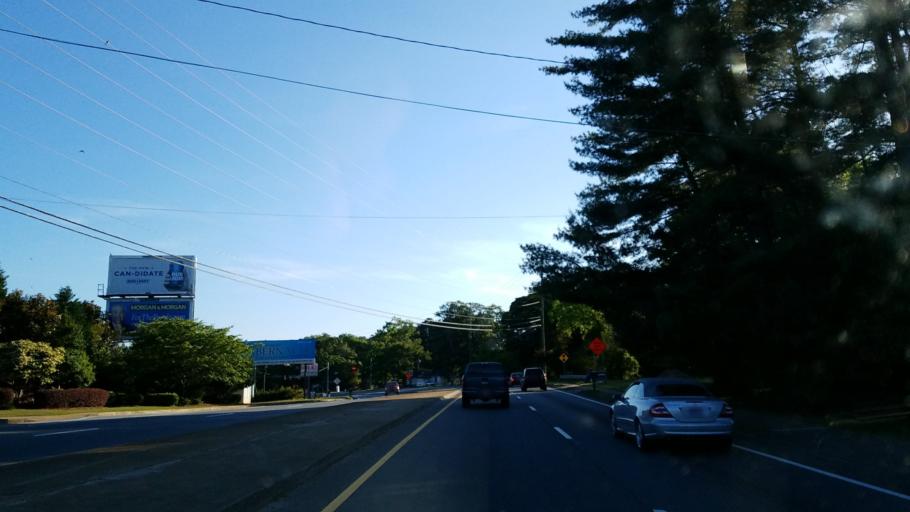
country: US
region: Georgia
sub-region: Cherokee County
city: Woodstock
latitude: 34.0976
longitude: -84.5815
